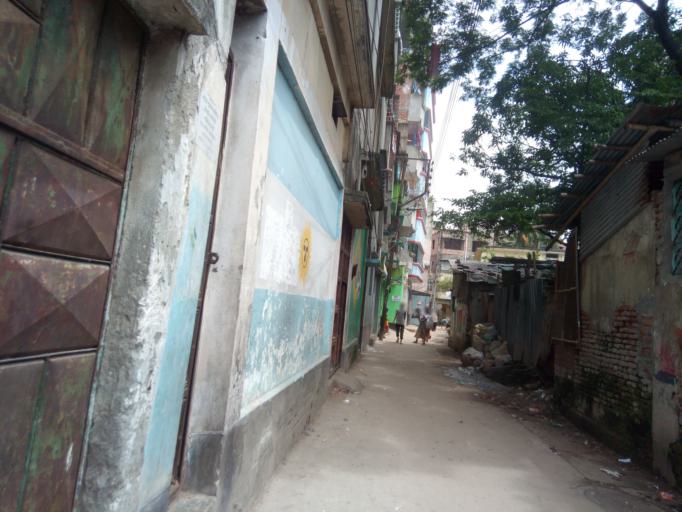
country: BD
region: Dhaka
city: Azimpur
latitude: 23.7286
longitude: 90.3724
